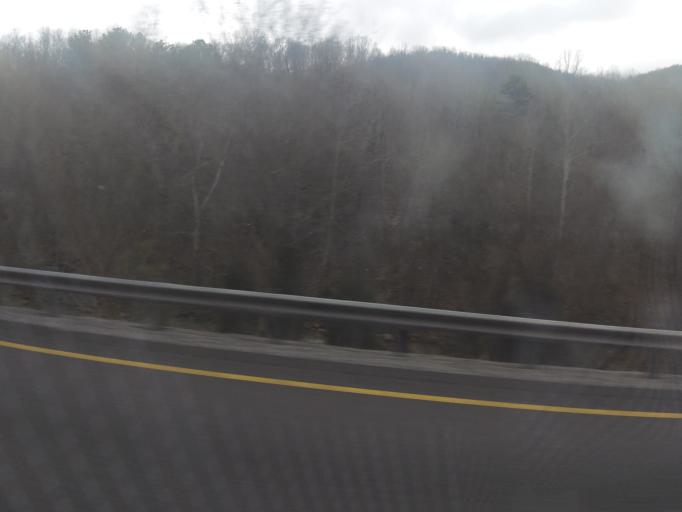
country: US
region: Tennessee
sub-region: Marion County
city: Jasper
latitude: 35.0059
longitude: -85.5224
